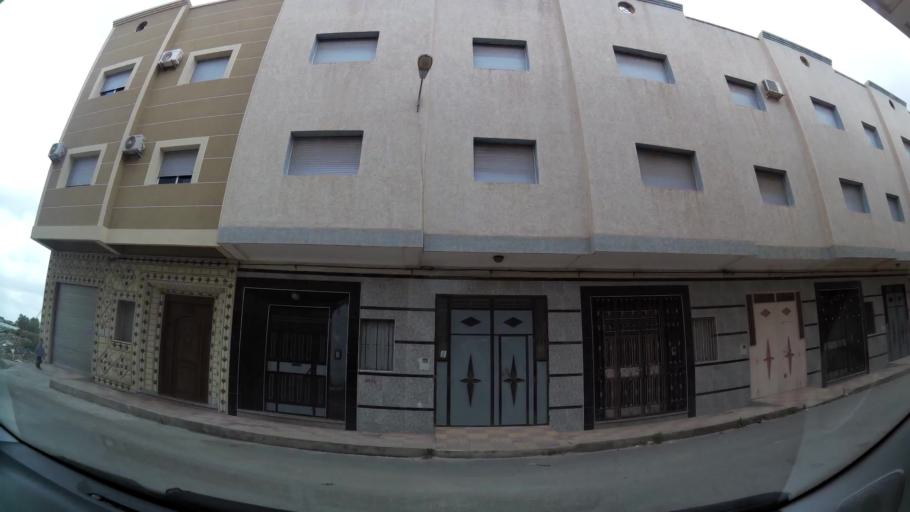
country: MA
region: Oriental
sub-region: Nador
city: Nador
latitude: 35.1633
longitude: -2.9127
